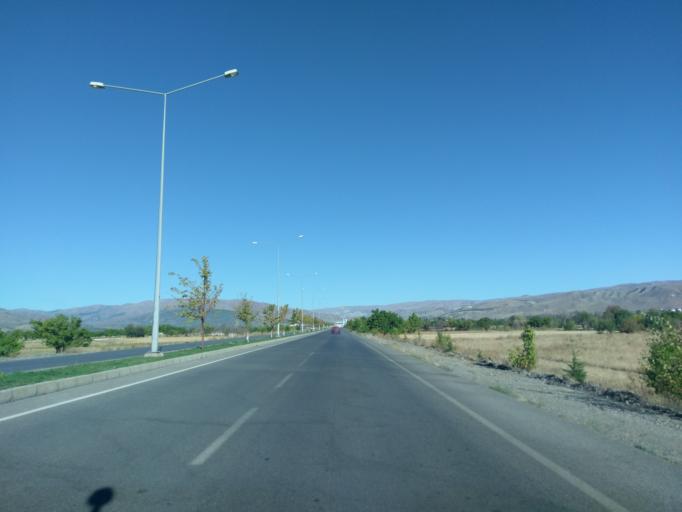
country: TR
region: Erzincan
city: Catalarmut
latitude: 39.7825
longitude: 39.4063
